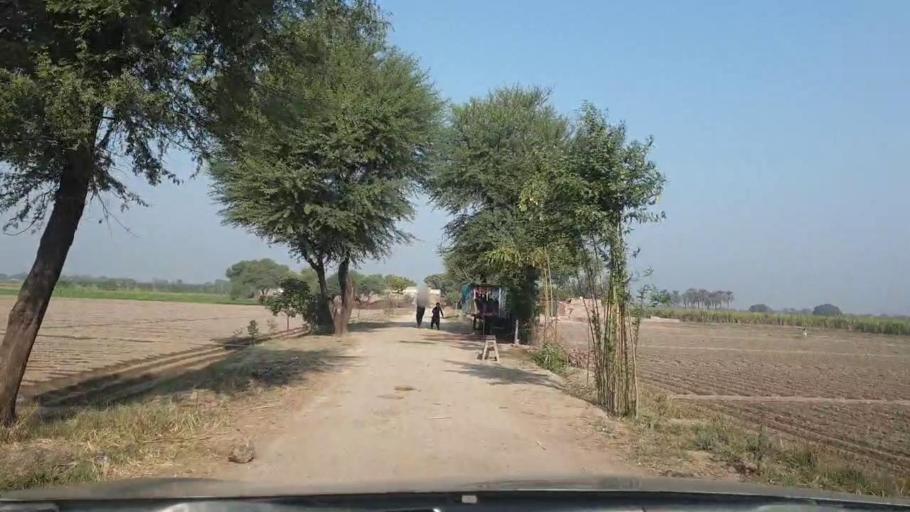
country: PK
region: Sindh
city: Tando Allahyar
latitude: 25.4930
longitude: 68.7511
